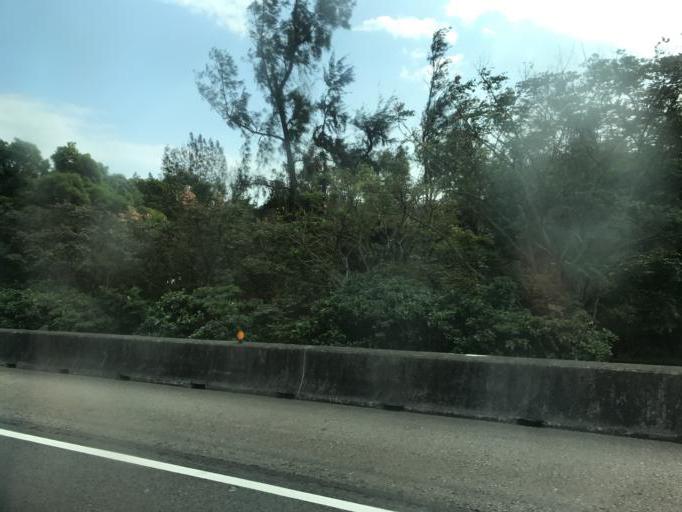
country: TW
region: Taiwan
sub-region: Hsinchu
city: Zhubei
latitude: 24.8769
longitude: 121.0426
